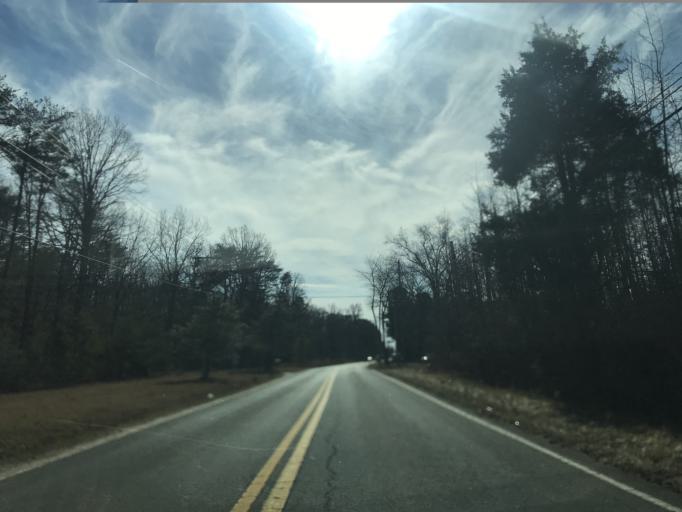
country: US
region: Maryland
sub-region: Charles County
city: Potomac Heights
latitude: 38.5607
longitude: -77.1288
